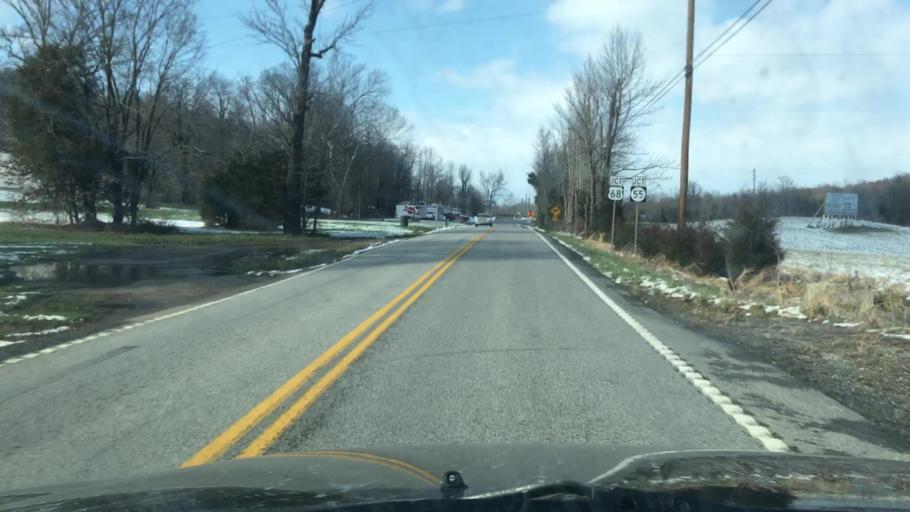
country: US
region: Kentucky
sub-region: Marion County
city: Lebanon
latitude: 37.5241
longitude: -85.3028
